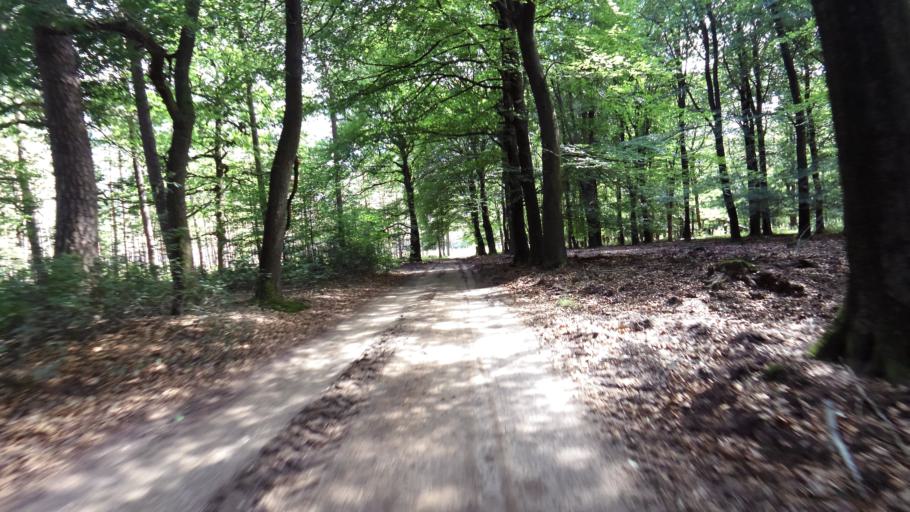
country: NL
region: Gelderland
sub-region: Gemeente Apeldoorn
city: Uddel
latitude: 52.2612
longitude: 5.8600
